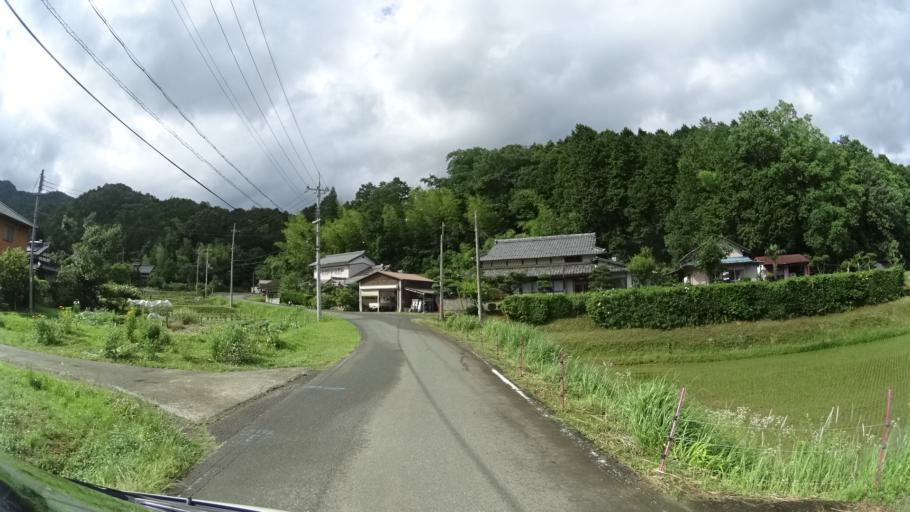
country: JP
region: Kyoto
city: Ayabe
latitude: 35.3856
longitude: 135.2383
